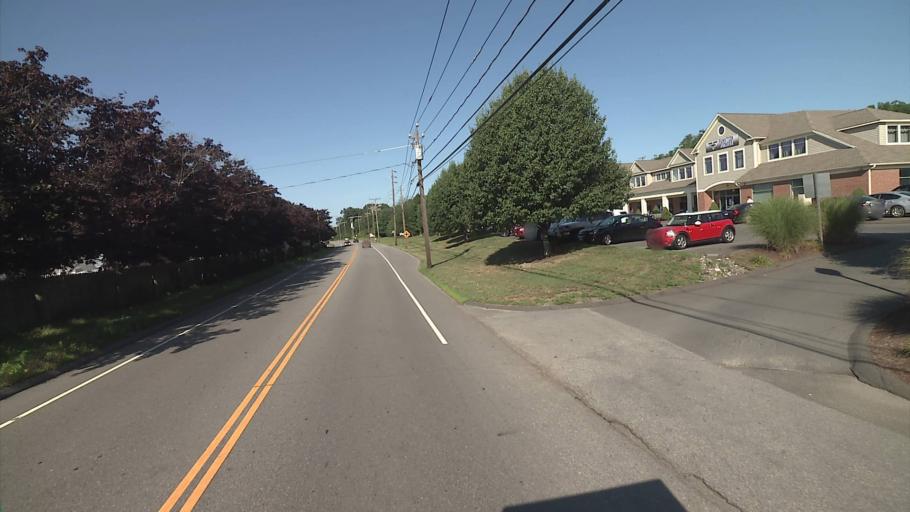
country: US
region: Connecticut
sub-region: Middlesex County
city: Clinton
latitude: 41.2775
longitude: -72.5408
